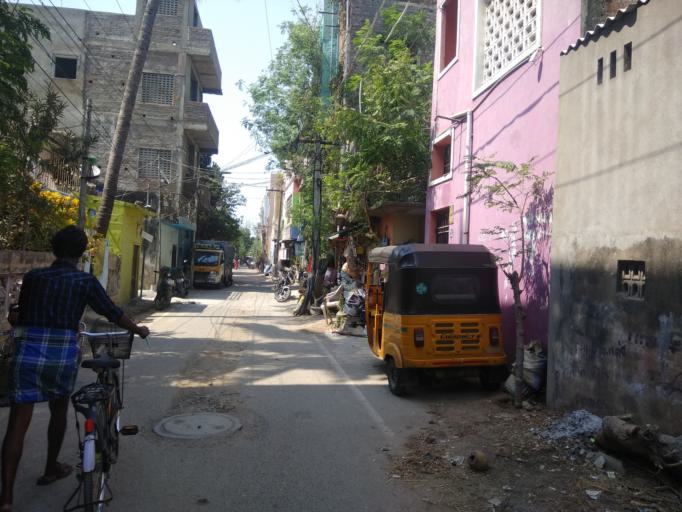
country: IN
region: Tamil Nadu
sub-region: Kancheepuram
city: Alandur
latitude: 12.9917
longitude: 80.2146
